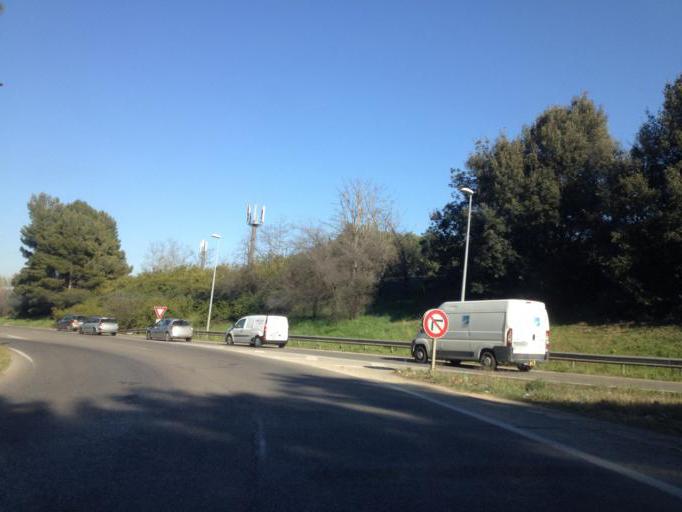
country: FR
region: Provence-Alpes-Cote d'Azur
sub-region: Departement des Bouches-du-Rhone
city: Bouc-Bel-Air
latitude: 43.5028
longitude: 5.3942
